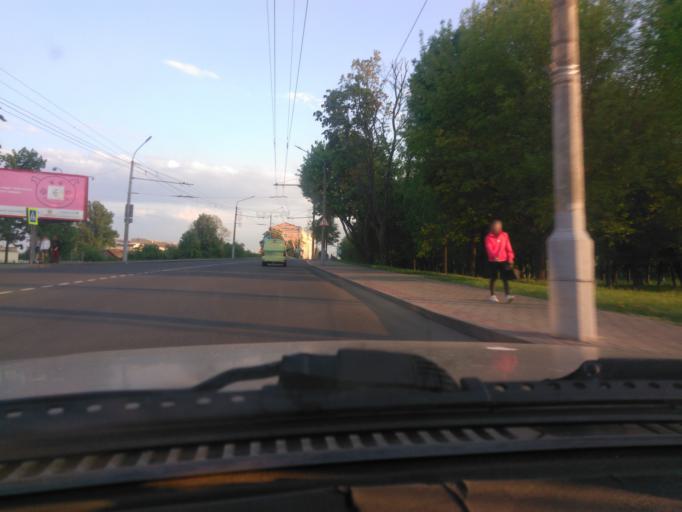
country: BY
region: Mogilev
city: Mahilyow
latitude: 53.9209
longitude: 30.3429
